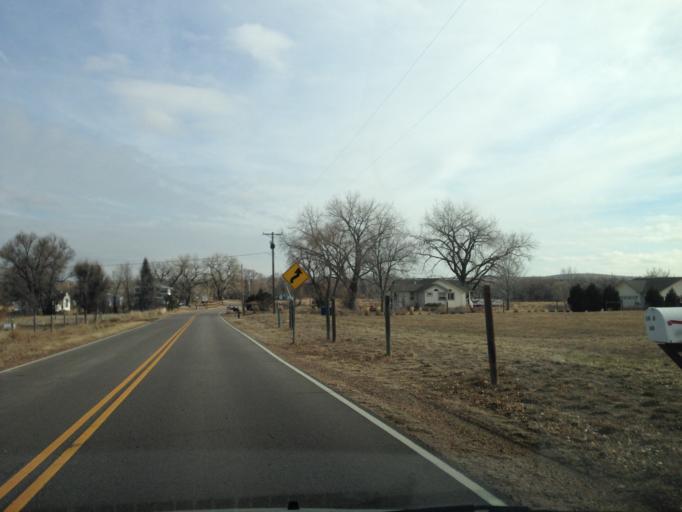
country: US
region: Colorado
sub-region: Boulder County
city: Lafayette
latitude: 39.9924
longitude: -105.0678
